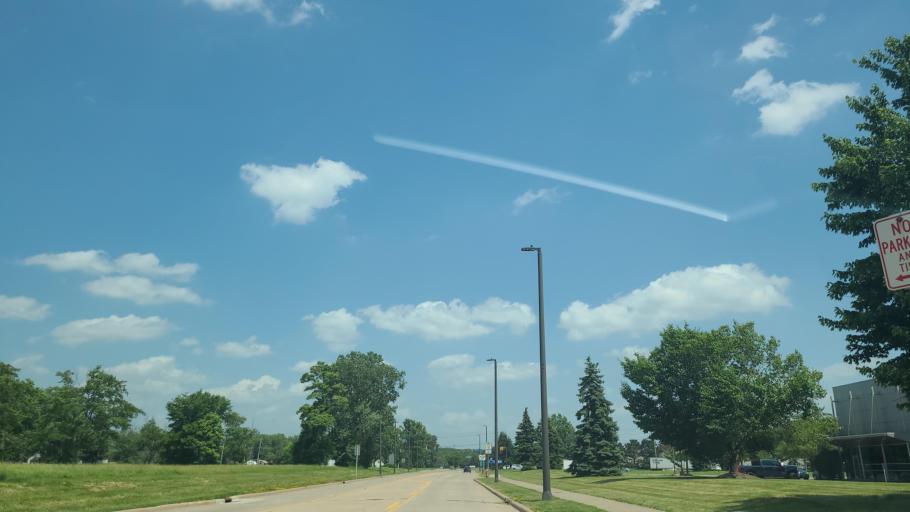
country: US
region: Ohio
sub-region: Cuyahoga County
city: Fairview Park
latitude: 41.4251
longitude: -81.8310
